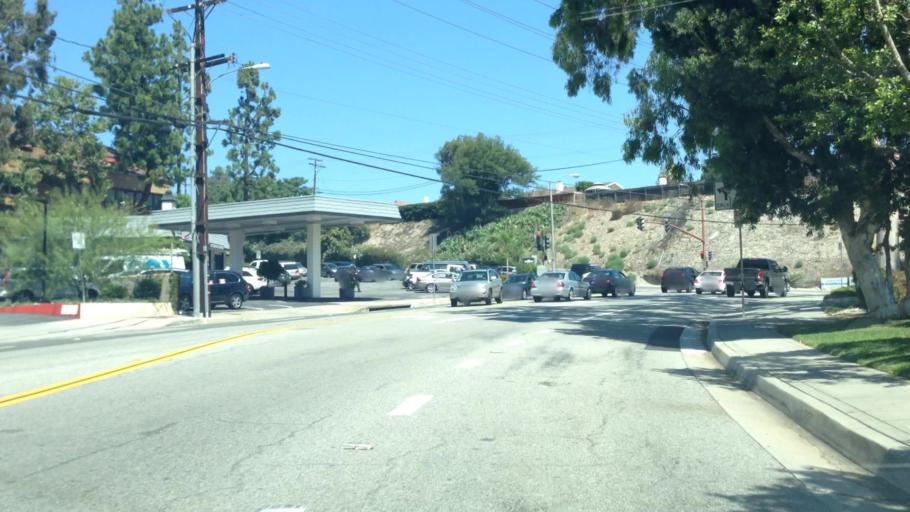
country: US
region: California
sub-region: Los Angeles County
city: Rolling Hills Estates
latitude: 33.7761
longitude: -118.3786
